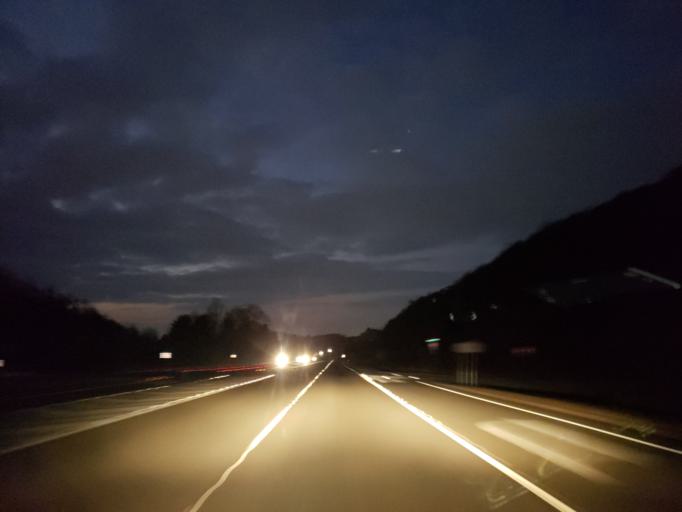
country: US
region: Georgia
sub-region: Polk County
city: Rockmart
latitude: 33.9849
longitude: -85.0169
